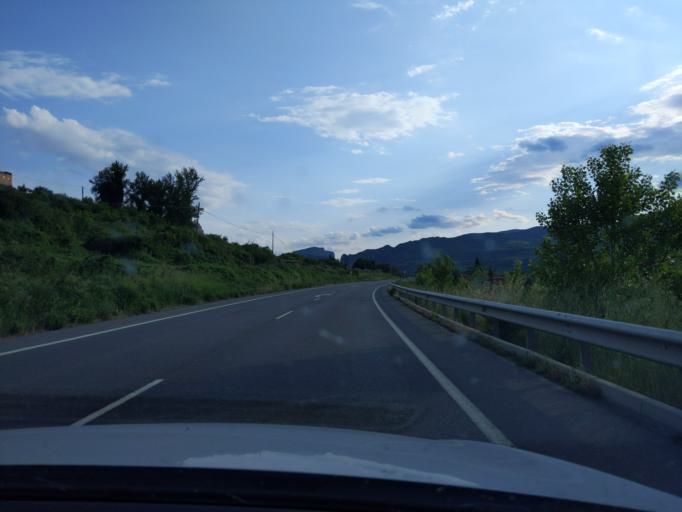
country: ES
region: La Rioja
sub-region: Provincia de La Rioja
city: Nalda
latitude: 42.3390
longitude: -2.4879
